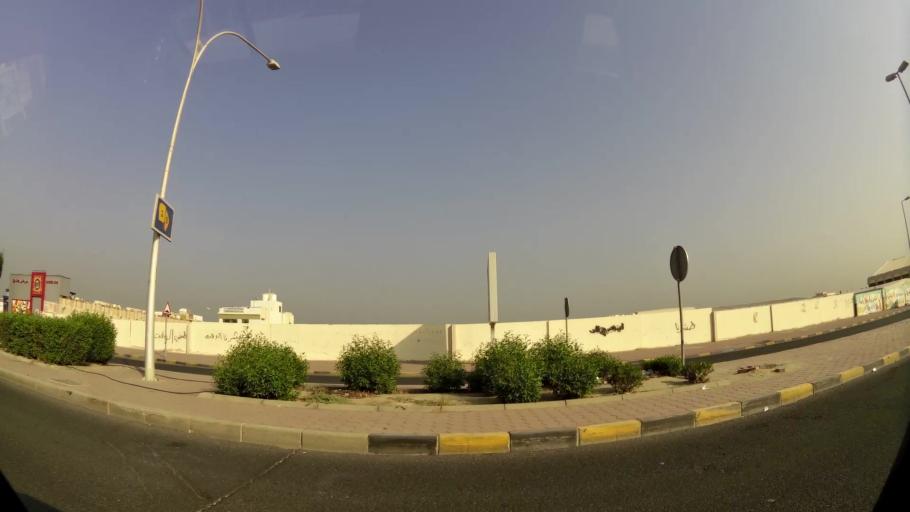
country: KW
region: Al Ahmadi
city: Al Manqaf
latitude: 29.1055
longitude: 48.1054
